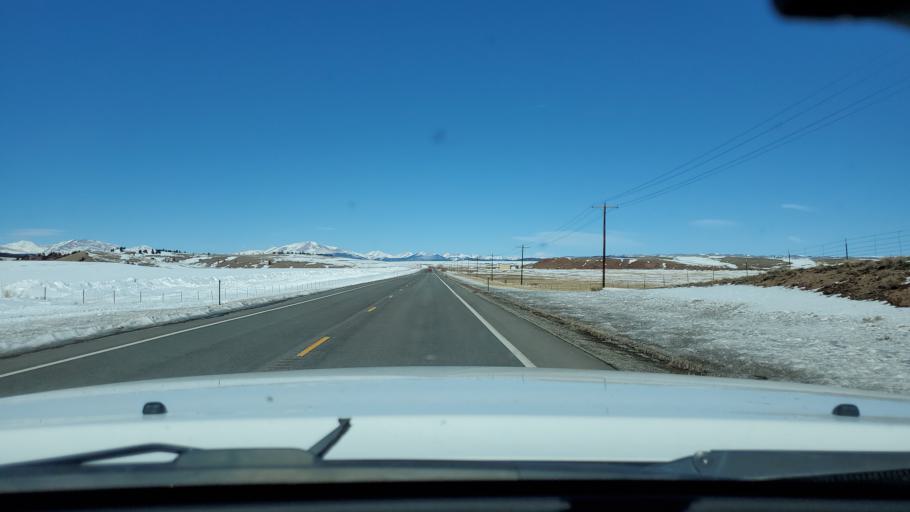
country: US
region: Colorado
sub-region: Park County
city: Fairplay
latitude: 39.0575
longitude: -105.9753
